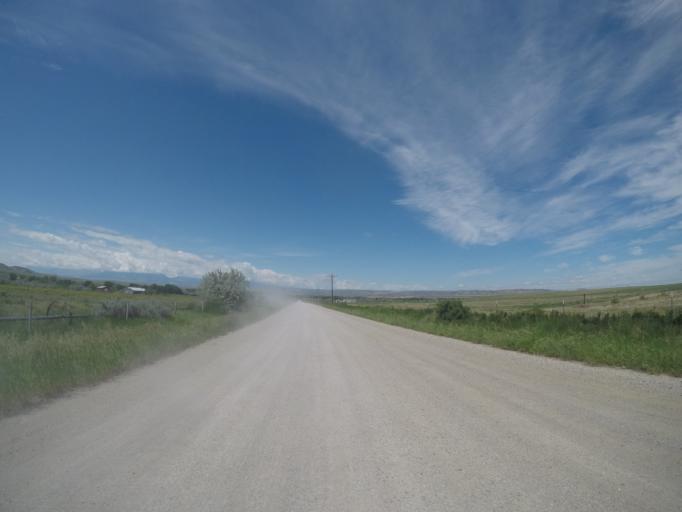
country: US
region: Montana
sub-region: Carbon County
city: Red Lodge
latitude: 45.2468
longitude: -108.8660
